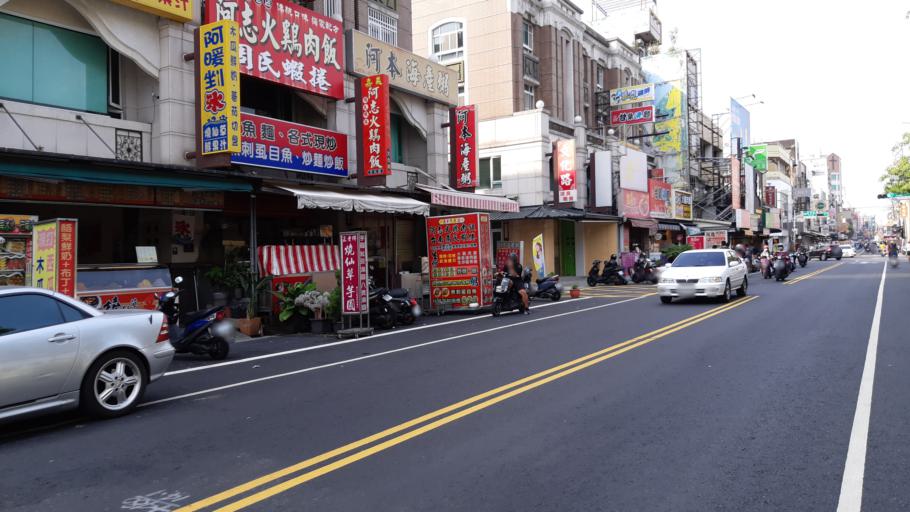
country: TW
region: Taiwan
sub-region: Chiayi
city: Jiayi Shi
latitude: 23.4752
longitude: 120.4502
